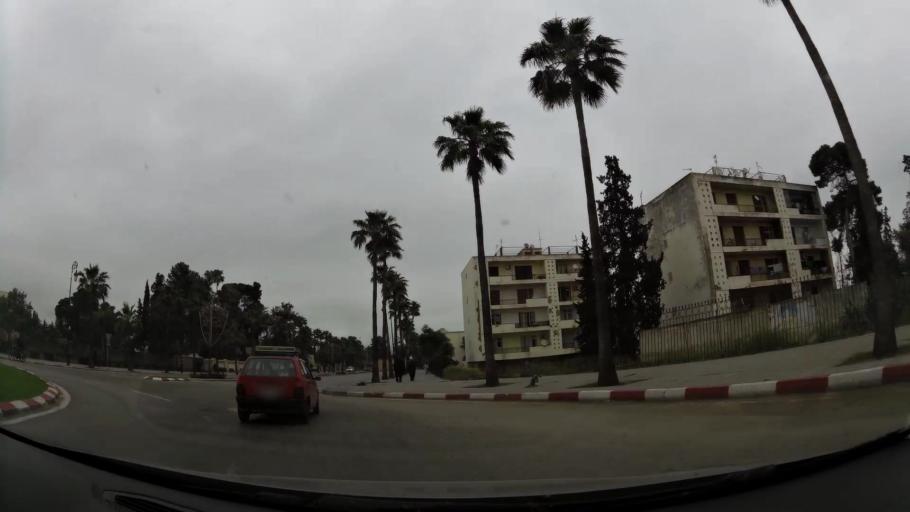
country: MA
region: Fes-Boulemane
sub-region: Fes
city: Fes
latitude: 34.0470
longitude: -4.9962
